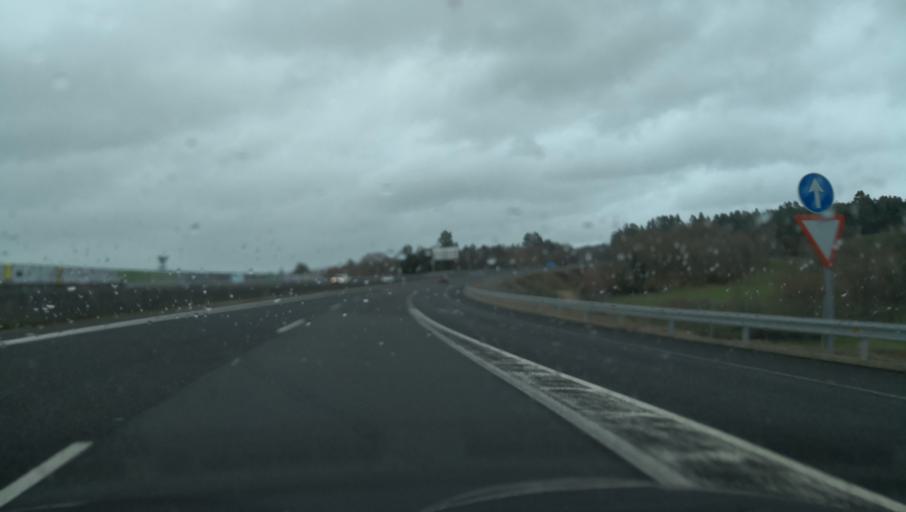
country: ES
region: Galicia
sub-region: Provincia de Pontevedra
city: Lalin
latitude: 42.6749
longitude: -8.1613
